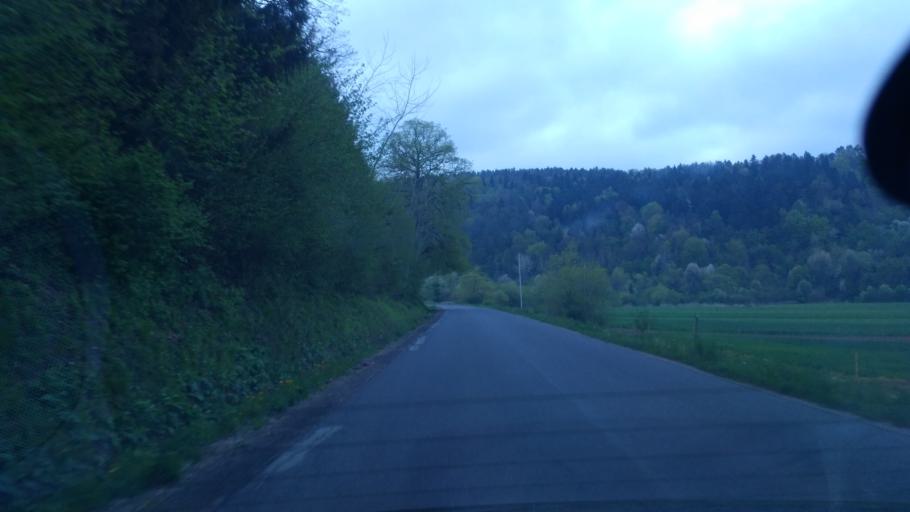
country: PL
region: Subcarpathian Voivodeship
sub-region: Powiat brzozowski
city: Nozdrzec
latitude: 49.7262
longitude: 22.2217
